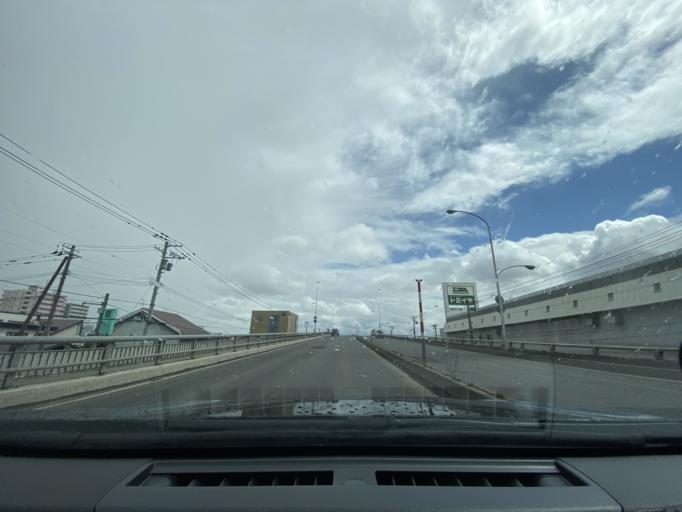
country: JP
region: Hokkaido
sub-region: Asahikawa-shi
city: Asahikawa
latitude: 43.8137
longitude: 142.4309
